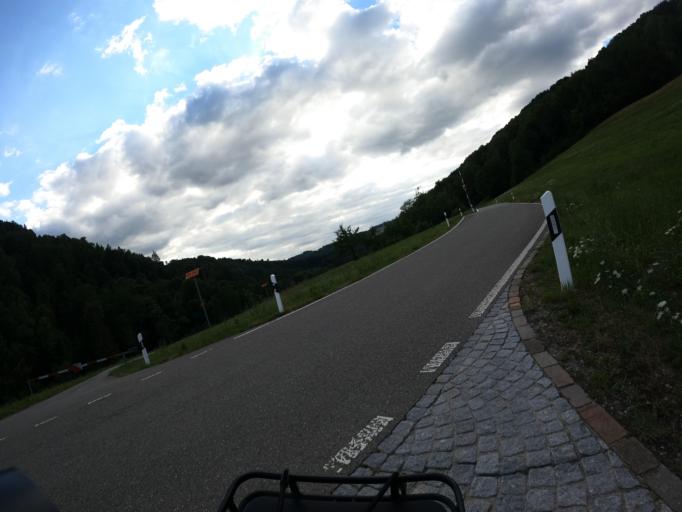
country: CH
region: Zurich
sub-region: Bezirk Dietikon
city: Urdorf / Oberurdorf
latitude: 47.3745
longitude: 8.4091
